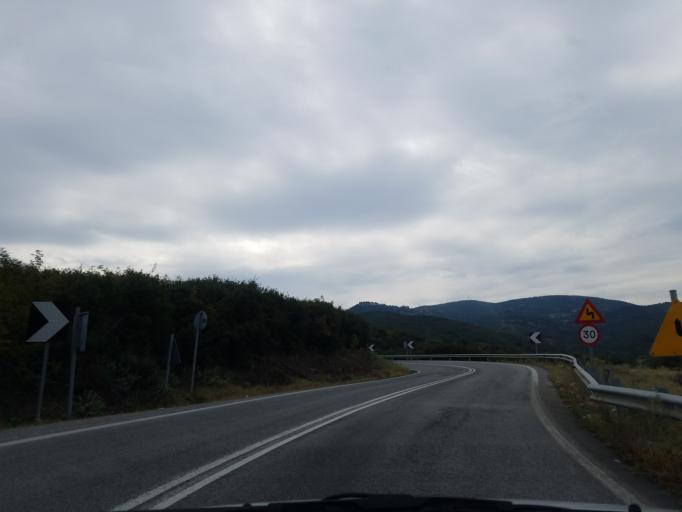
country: GR
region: Central Greece
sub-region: Nomos Fthiotidos
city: Domokos
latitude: 39.1535
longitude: 22.2975
